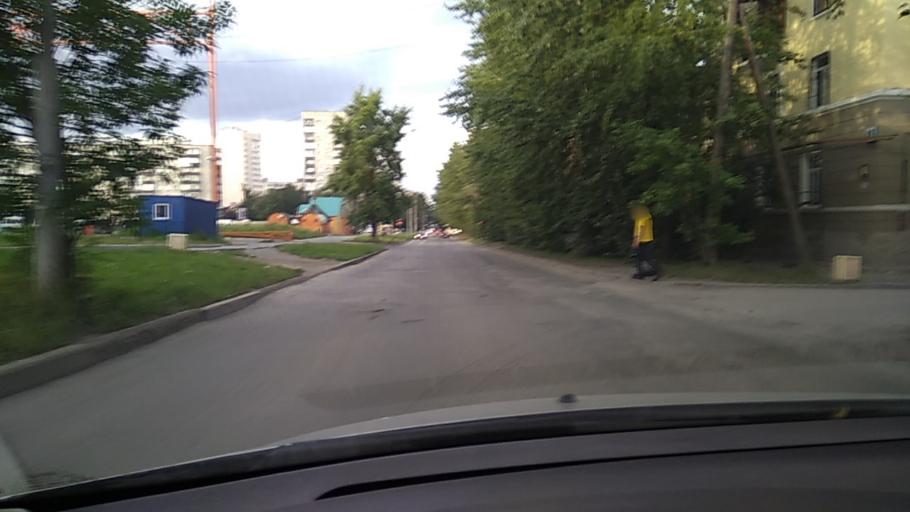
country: RU
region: Sverdlovsk
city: Yekaterinburg
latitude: 56.9005
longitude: 60.5893
